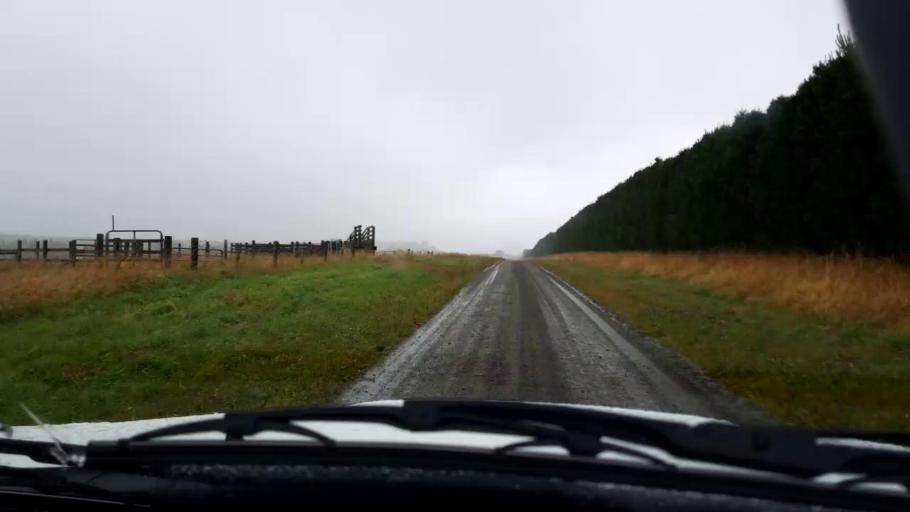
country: NZ
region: Canterbury
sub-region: Timaru District
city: Pleasant Point
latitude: -44.1690
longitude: 171.1543
